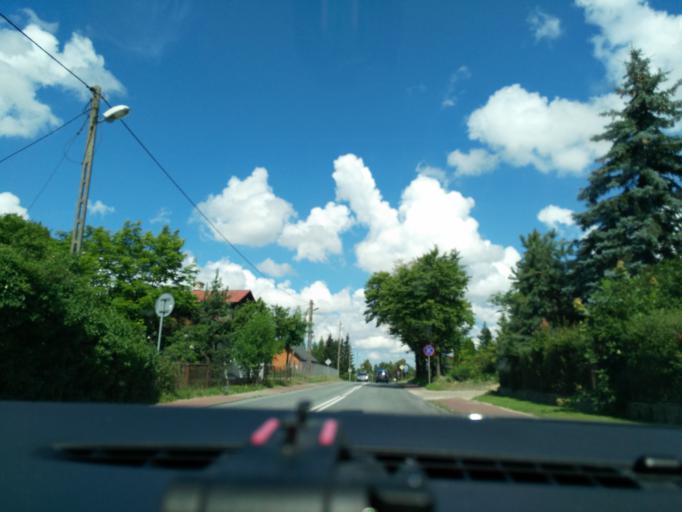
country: PL
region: Masovian Voivodeship
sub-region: Powiat losicki
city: Sarnaki
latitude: 52.3174
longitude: 22.8868
